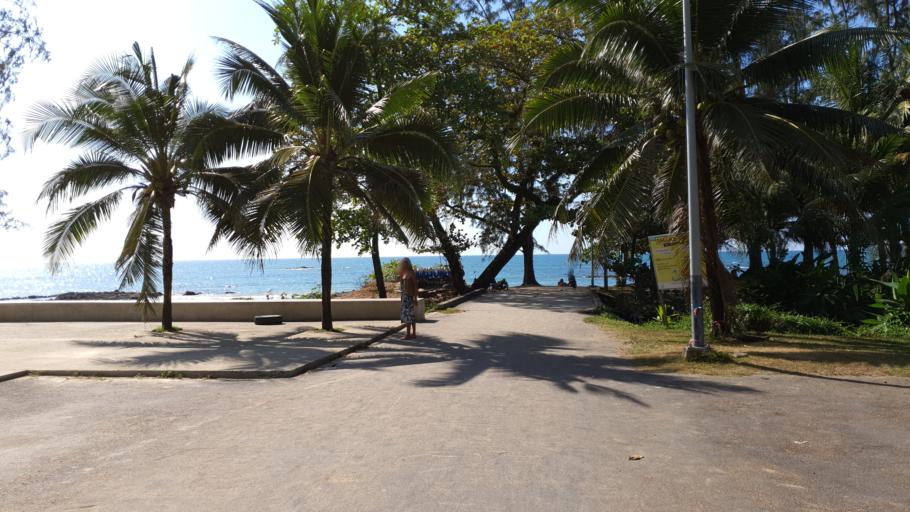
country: TH
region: Phangnga
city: Ban Khao Lak
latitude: 8.6452
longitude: 98.2471
